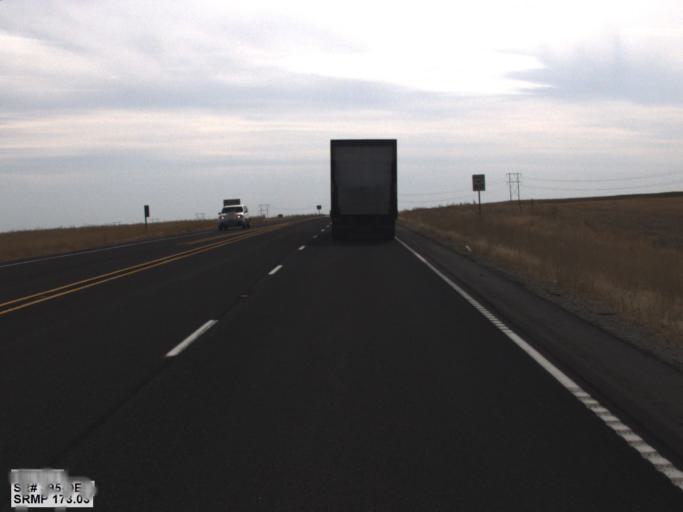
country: US
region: Washington
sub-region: Spokane County
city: Fairwood
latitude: 47.8593
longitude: -117.4219
